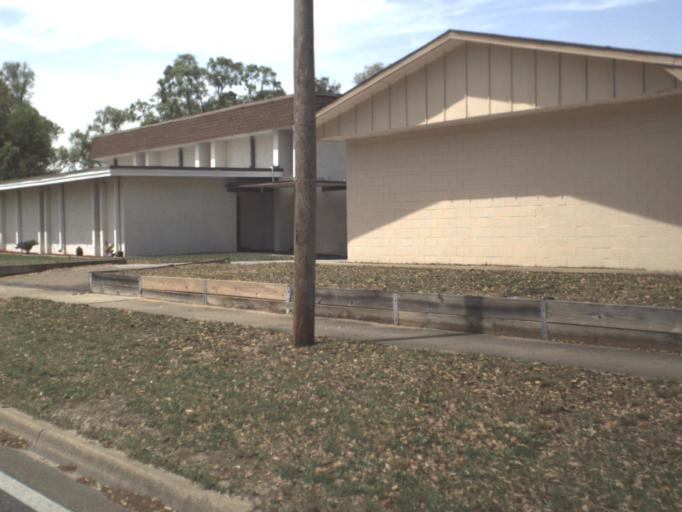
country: US
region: Florida
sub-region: Escambia County
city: Bellview
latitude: 30.4610
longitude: -87.2921
